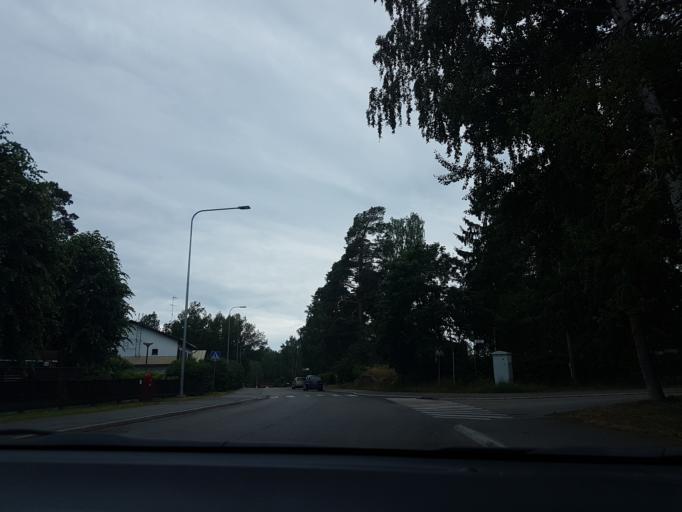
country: FI
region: Uusimaa
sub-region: Helsinki
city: Vantaa
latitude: 60.2125
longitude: 25.1278
